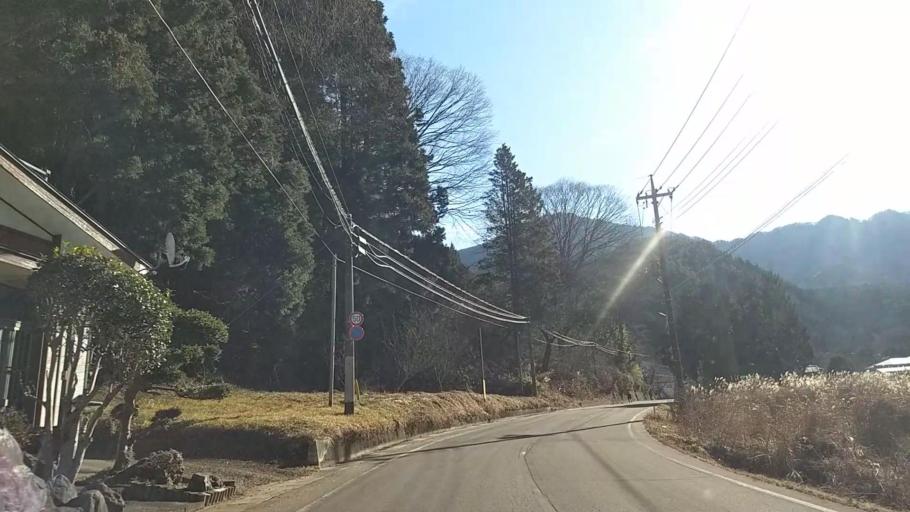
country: JP
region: Yamanashi
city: Otsuki
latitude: 35.5224
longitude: 138.9262
